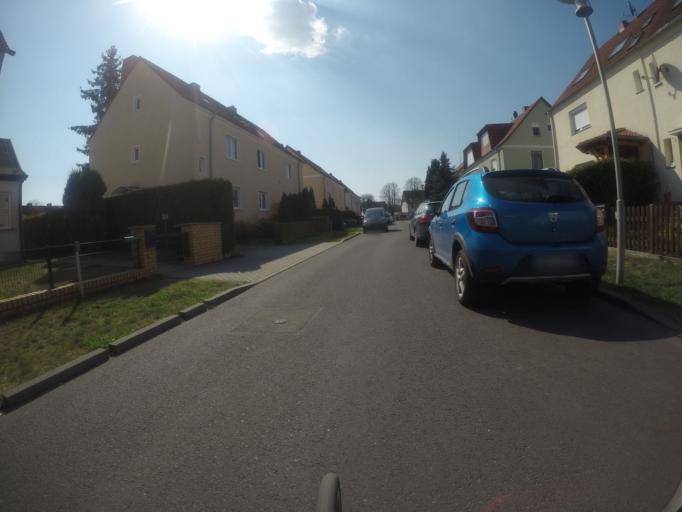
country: DE
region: Brandenburg
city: Hennigsdorf
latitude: 52.6426
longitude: 13.1912
